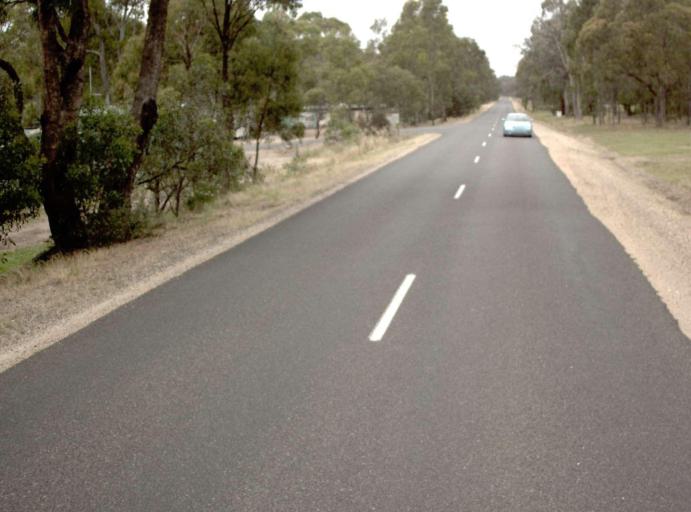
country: AU
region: Victoria
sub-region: Wellington
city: Heyfield
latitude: -37.9193
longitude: 146.7553
